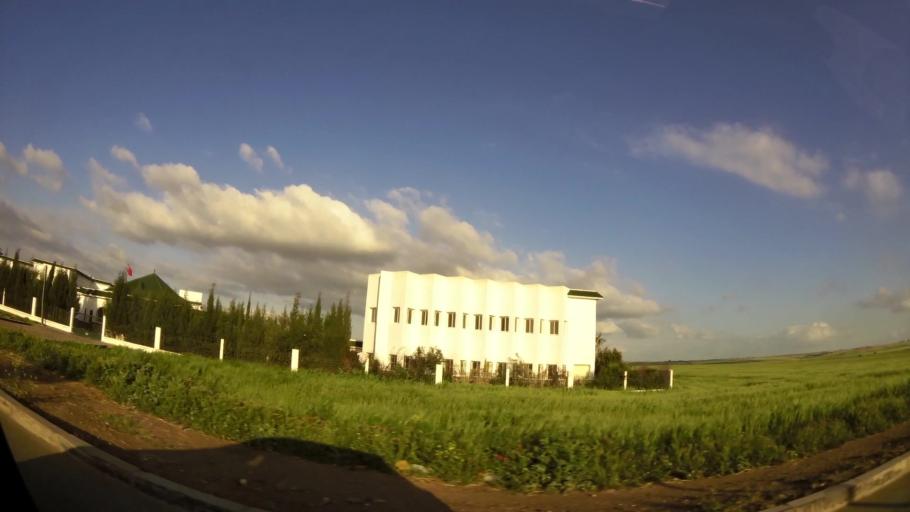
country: MA
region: Chaouia-Ouardigha
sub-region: Settat Province
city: Settat
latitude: 33.0055
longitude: -7.5951
